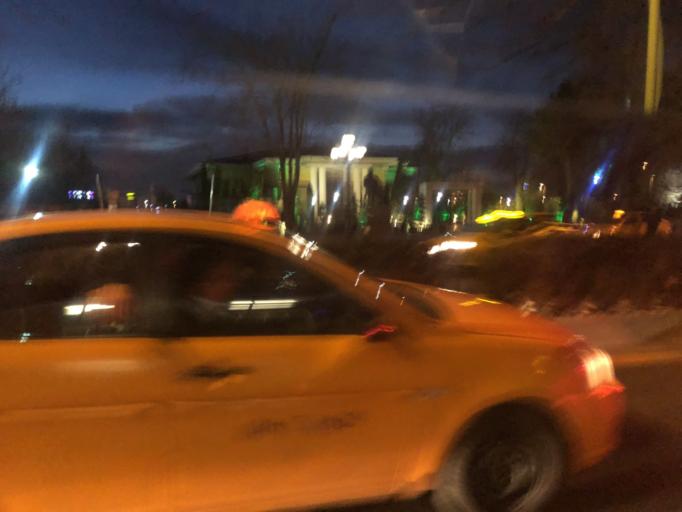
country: TR
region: Ankara
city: Ankara
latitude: 39.9360
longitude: 32.8543
